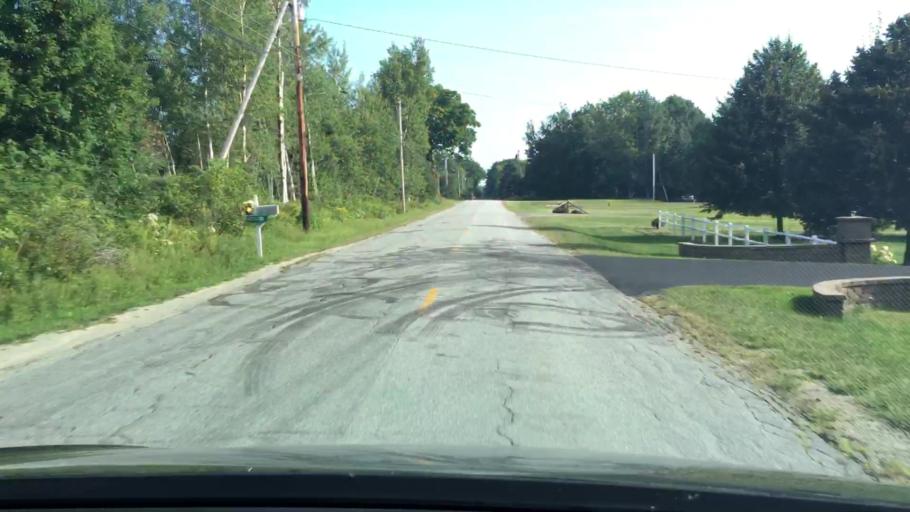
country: US
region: Maine
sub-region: Hancock County
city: Bucksport
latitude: 44.5442
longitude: -68.7965
